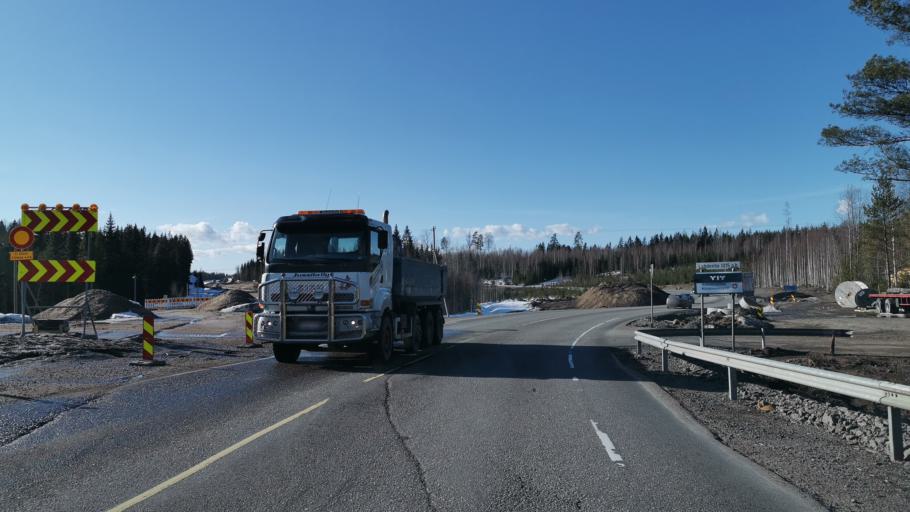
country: FI
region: Kymenlaakso
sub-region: Kouvola
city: Kouvola
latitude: 60.8677
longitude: 26.5528
